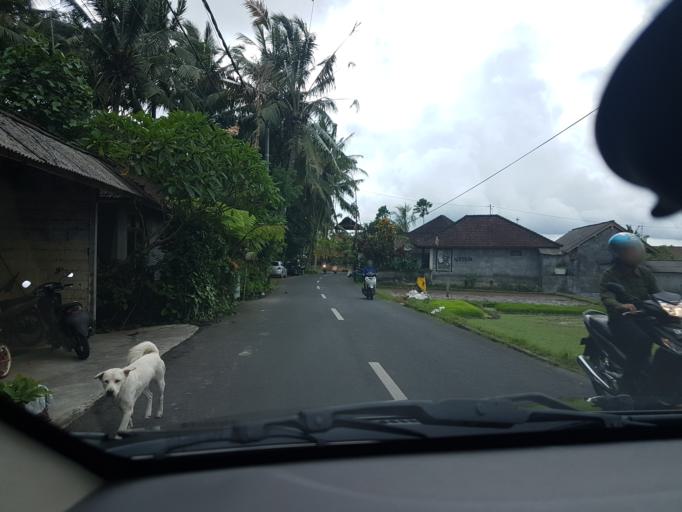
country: ID
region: Bali
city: Banjar Triwangsakeliki
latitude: -8.4588
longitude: 115.2744
